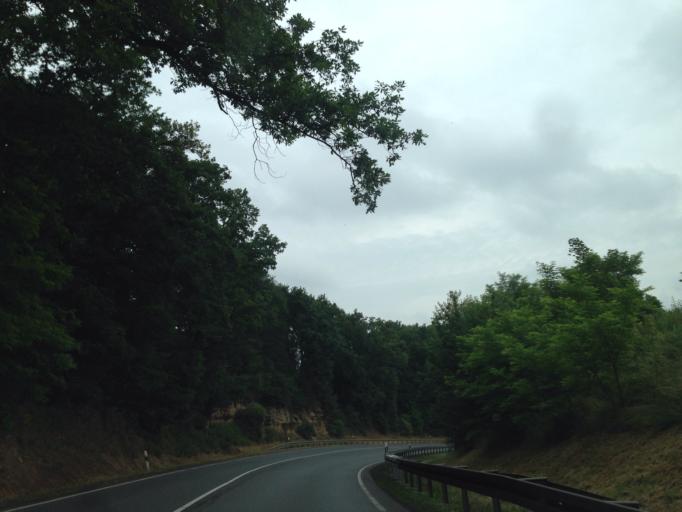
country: DE
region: Thuringia
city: Bad Blankenburg
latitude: 50.6744
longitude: 11.3201
